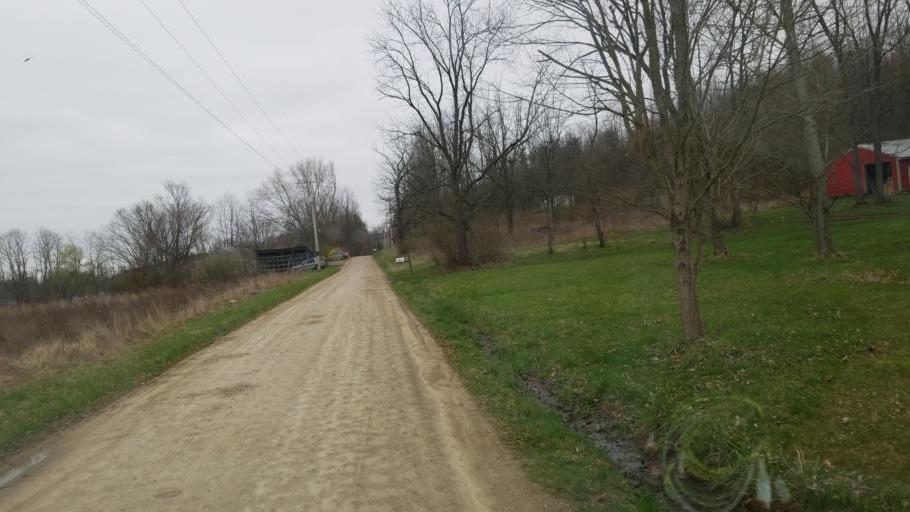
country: US
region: Ohio
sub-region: Knox County
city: Gambier
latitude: 40.4702
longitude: -82.4114
